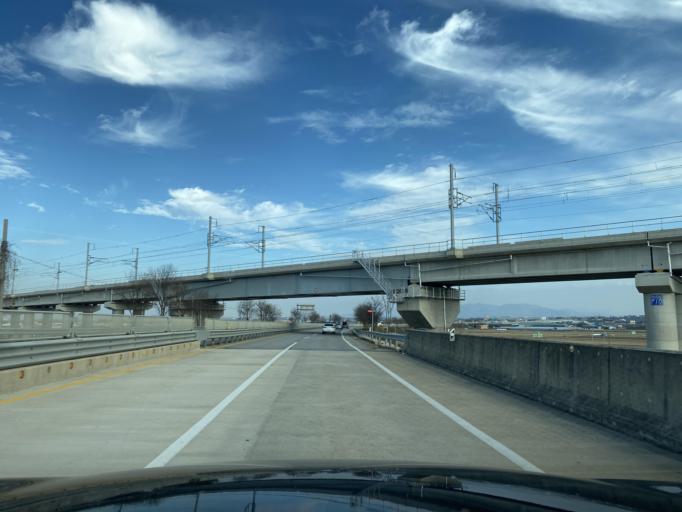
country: KR
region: Chungcheongnam-do
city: Hongsung
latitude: 36.6913
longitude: 126.7239
